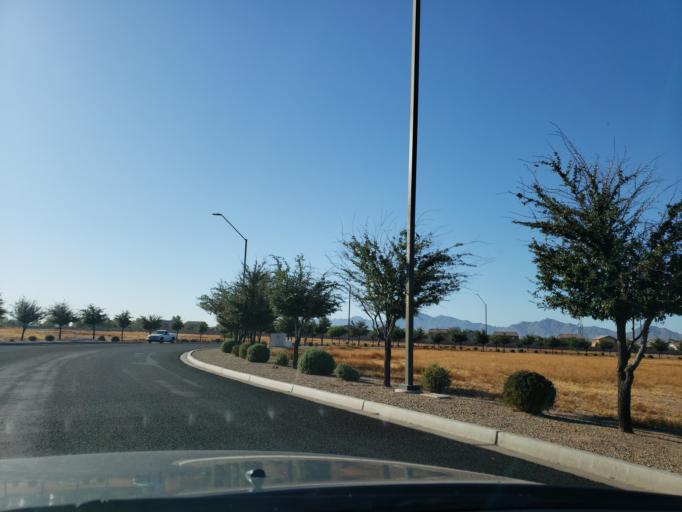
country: US
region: Arizona
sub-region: Maricopa County
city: Tolleson
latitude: 33.4450
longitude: -112.3015
